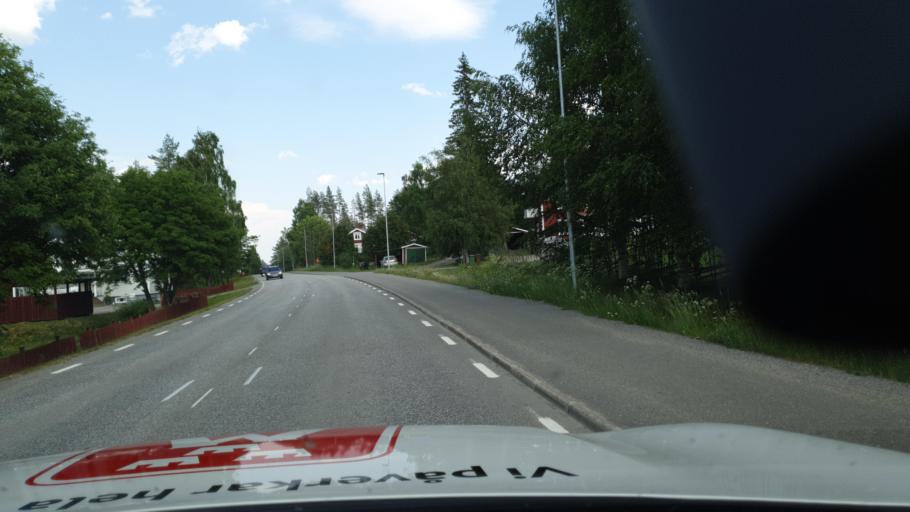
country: SE
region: Vaesterbotten
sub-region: Skelleftea Kommun
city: Viken
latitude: 64.7320
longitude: 20.7326
